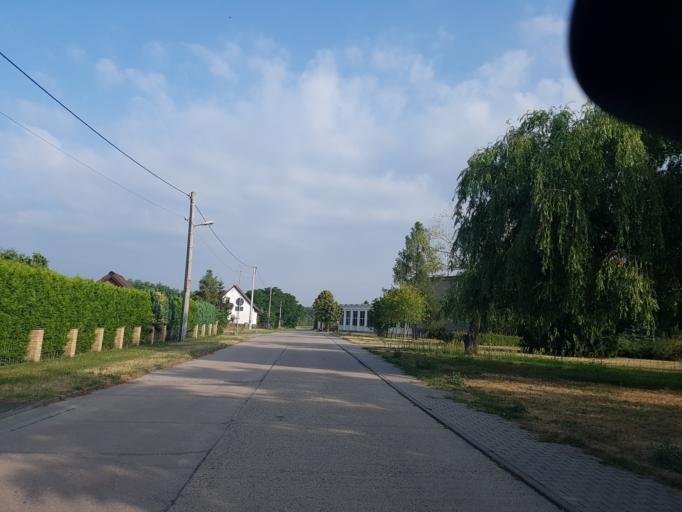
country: DE
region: Saxony-Anhalt
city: Holzdorf
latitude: 51.8590
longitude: 13.1017
